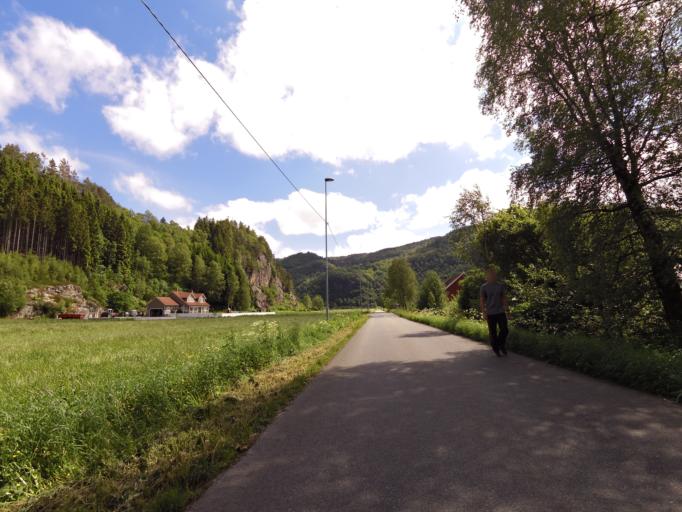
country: NO
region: Vest-Agder
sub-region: Kvinesdal
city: Liknes
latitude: 58.3053
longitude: 6.9441
